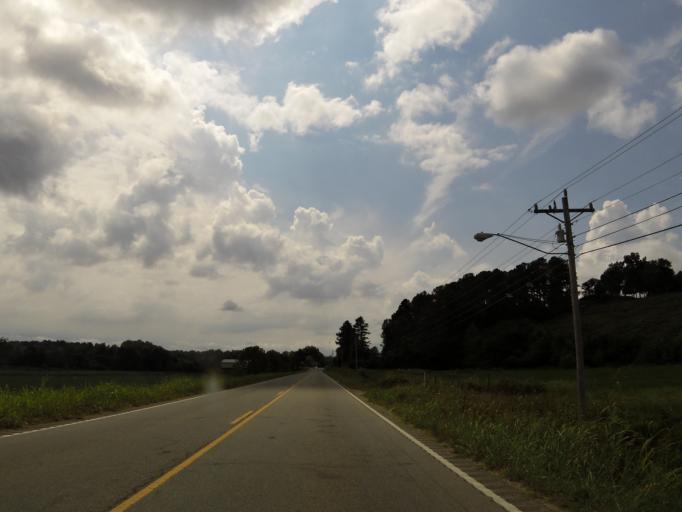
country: US
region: Tennessee
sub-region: Perry County
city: Linden
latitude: 35.6260
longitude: -87.8348
